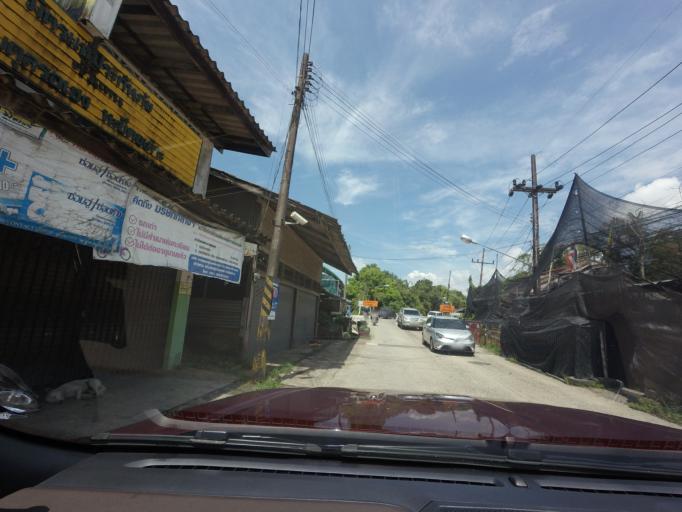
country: TH
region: Narathiwat
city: Ra-ngae
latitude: 6.2887
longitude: 101.7058
